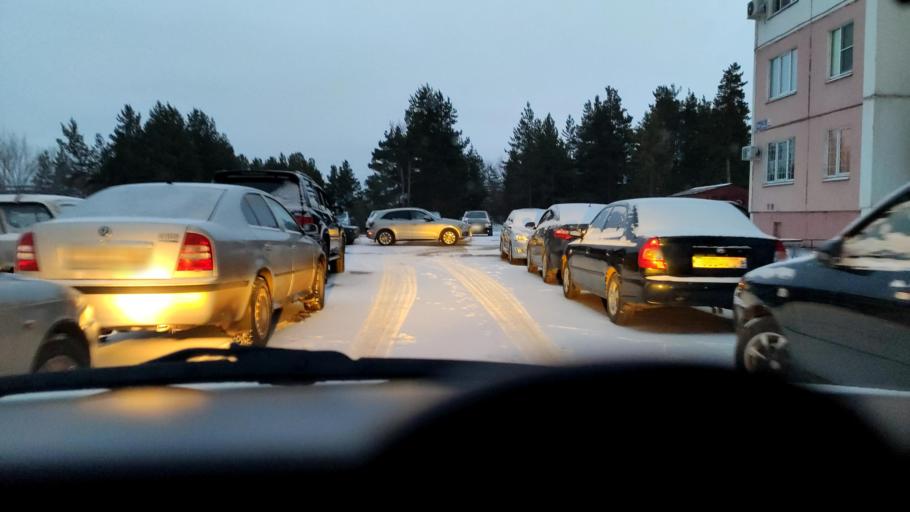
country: RU
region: Voronezj
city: Pridonskoy
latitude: 51.7060
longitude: 39.1072
